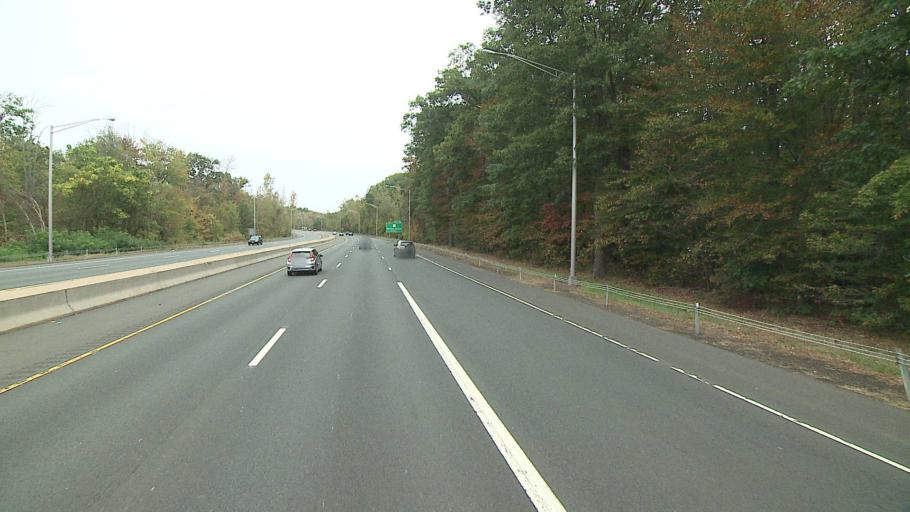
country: US
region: Connecticut
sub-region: Hartford County
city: Newington
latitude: 41.7043
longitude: -72.7576
